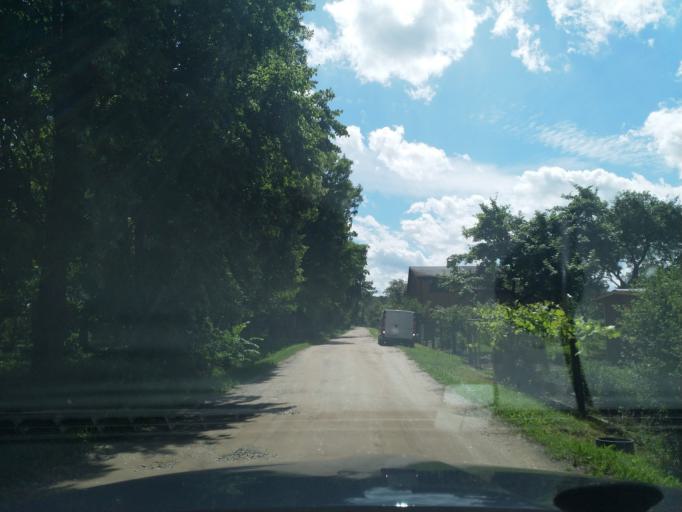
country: LV
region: Kuldigas Rajons
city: Kuldiga
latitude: 56.9538
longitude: 22.0007
